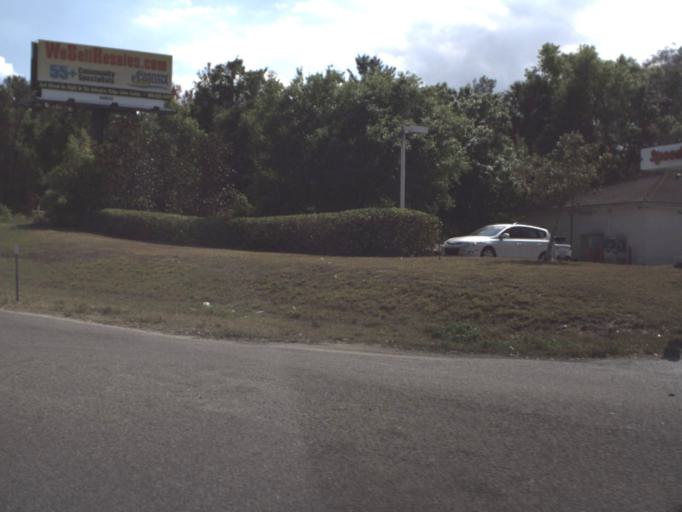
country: US
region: Florida
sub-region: Lake County
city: Hawthorne
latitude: 28.7463
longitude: -81.8766
